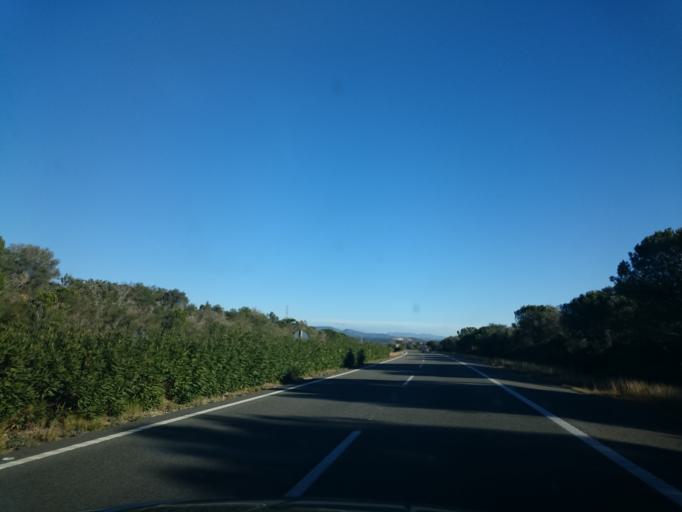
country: ES
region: Catalonia
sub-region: Provincia de Tarragona
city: Masdenverge
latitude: 40.7067
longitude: 0.5508
